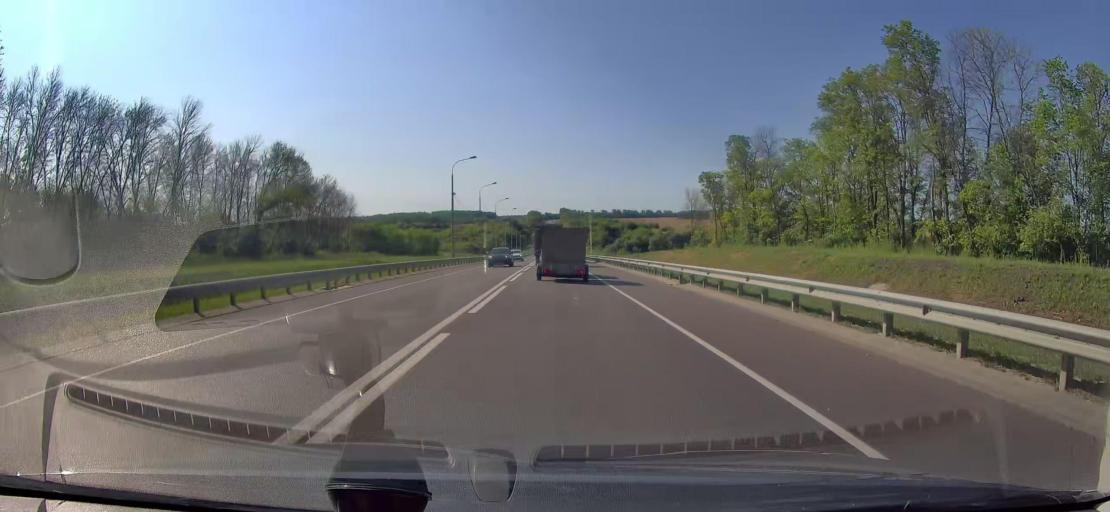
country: RU
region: Orjol
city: Kromy
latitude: 52.6247
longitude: 35.7570
